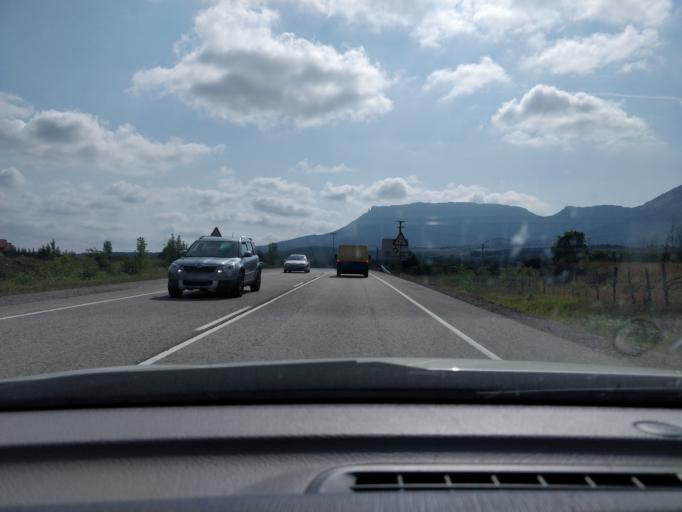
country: ES
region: Castille and Leon
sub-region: Provincia de Burgos
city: Villasana de Mena
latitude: 43.0939
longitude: -3.2923
